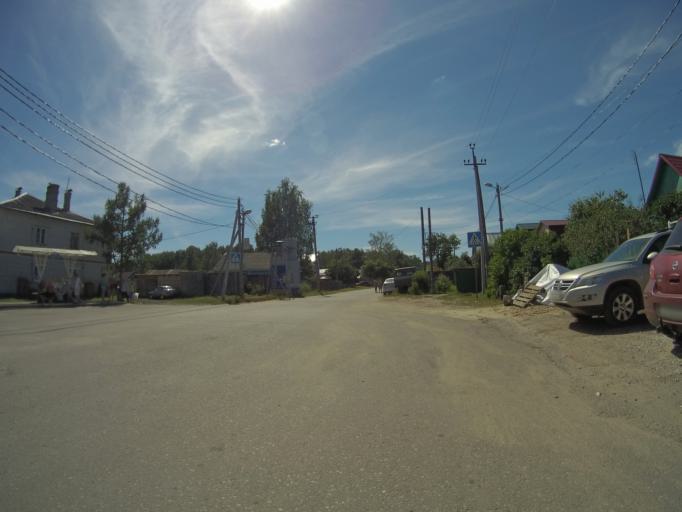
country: RU
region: Vladimir
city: Raduzhnyy
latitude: 56.0574
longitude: 40.3655
